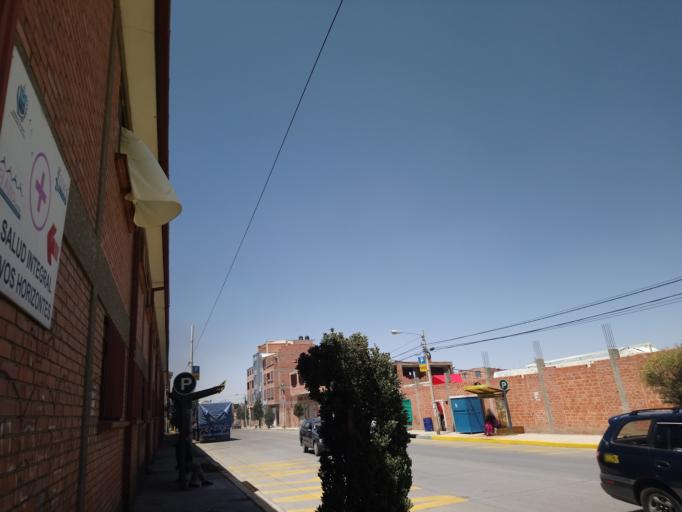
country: BO
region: La Paz
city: La Paz
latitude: -16.5434
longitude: -68.1912
